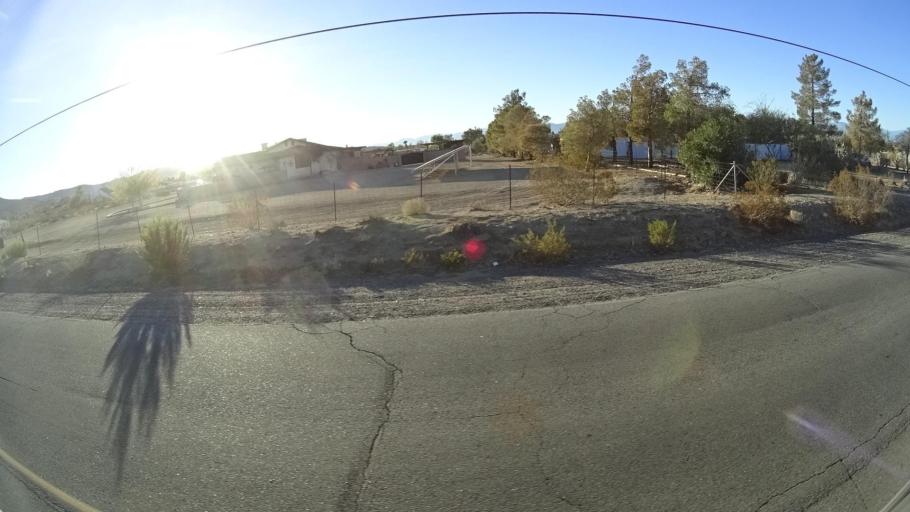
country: US
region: California
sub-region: Kern County
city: Ridgecrest
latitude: 35.5883
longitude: -117.6527
